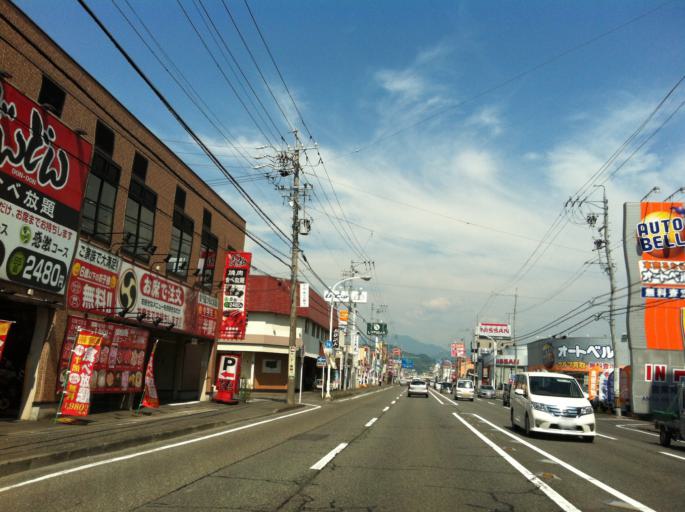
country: JP
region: Shizuoka
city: Shizuoka-shi
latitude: 34.9947
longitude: 138.4139
